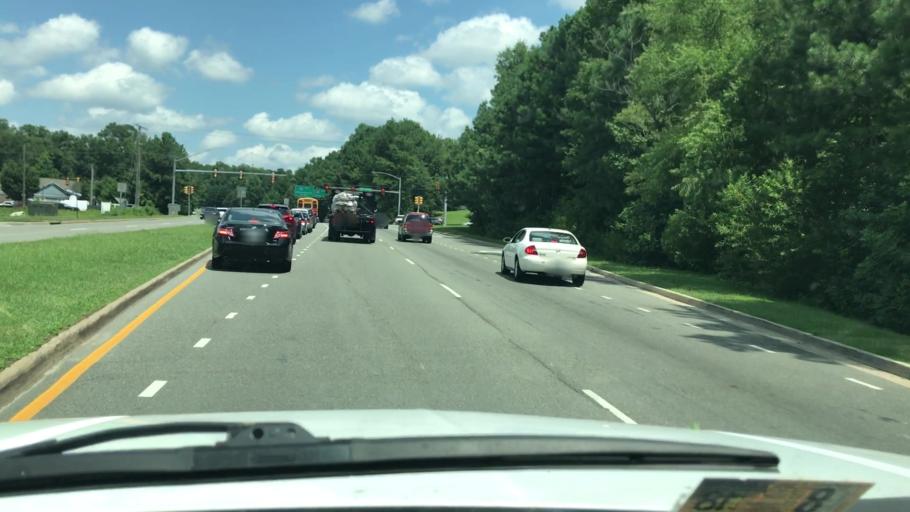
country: US
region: Virginia
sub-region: Henrico County
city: Short Pump
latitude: 37.6299
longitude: -77.5786
